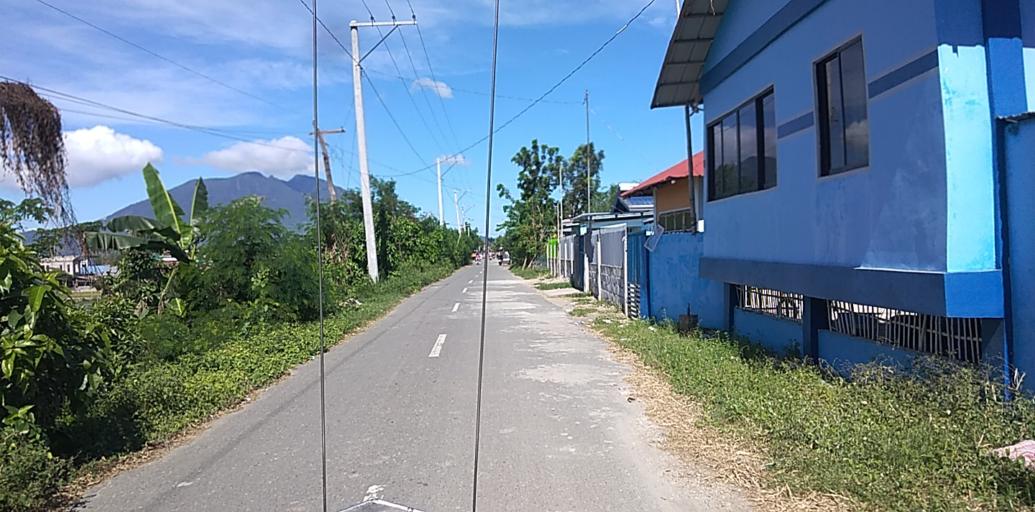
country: PH
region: Central Luzon
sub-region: Province of Pampanga
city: Candating
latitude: 15.1308
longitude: 120.8082
